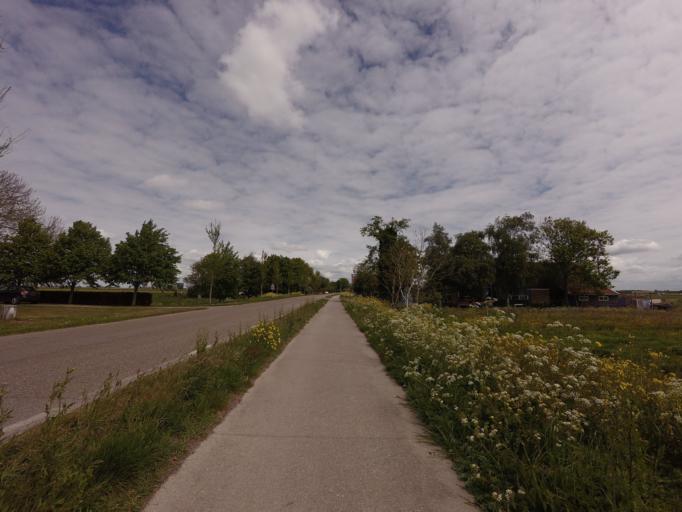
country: NL
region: Friesland
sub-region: Gemeente Gaasterlan-Sleat
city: Oudemirdum
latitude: 52.8943
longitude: 5.5035
